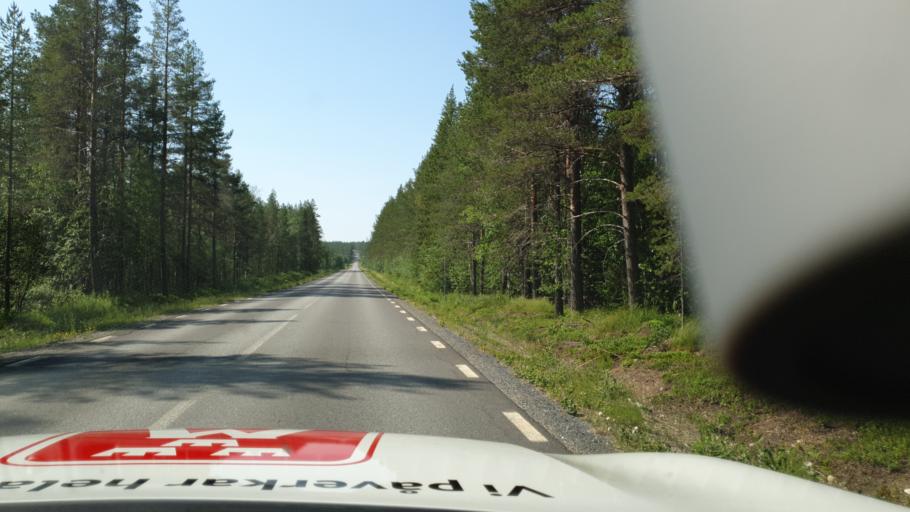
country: SE
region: Vaesterbotten
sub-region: Skelleftea Kommun
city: Langsele
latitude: 64.9848
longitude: 20.0741
